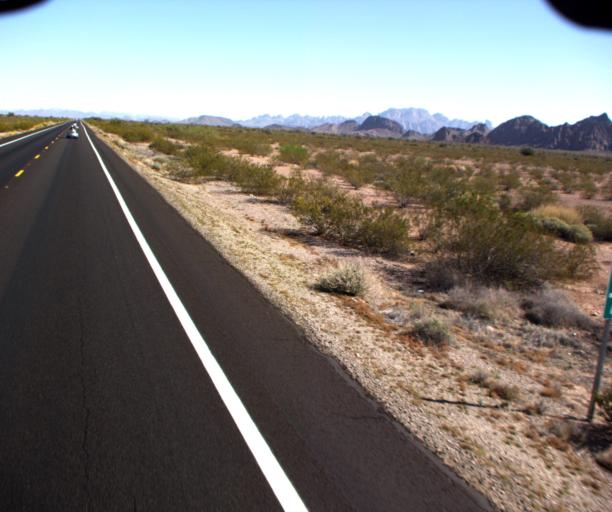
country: US
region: Arizona
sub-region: La Paz County
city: Quartzsite
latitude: 33.2708
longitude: -114.2370
